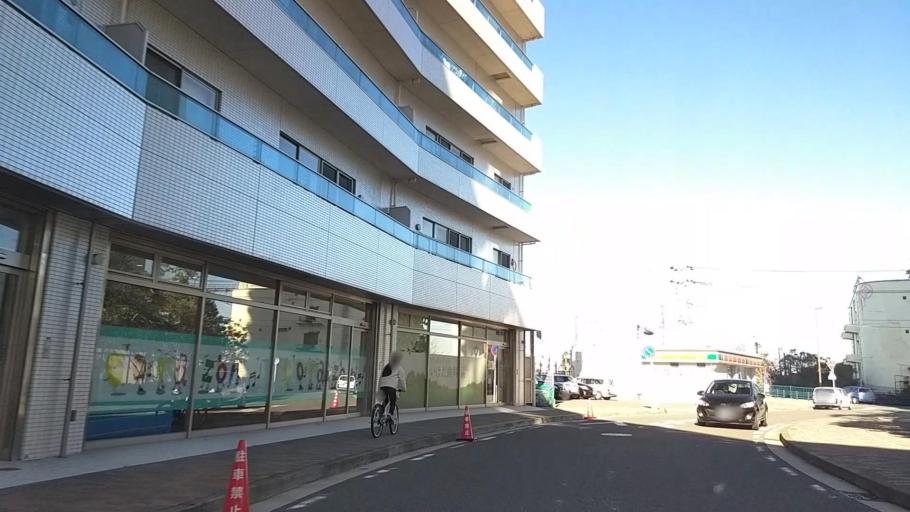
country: JP
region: Kanagawa
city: Yokohama
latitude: 35.4717
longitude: 139.6375
